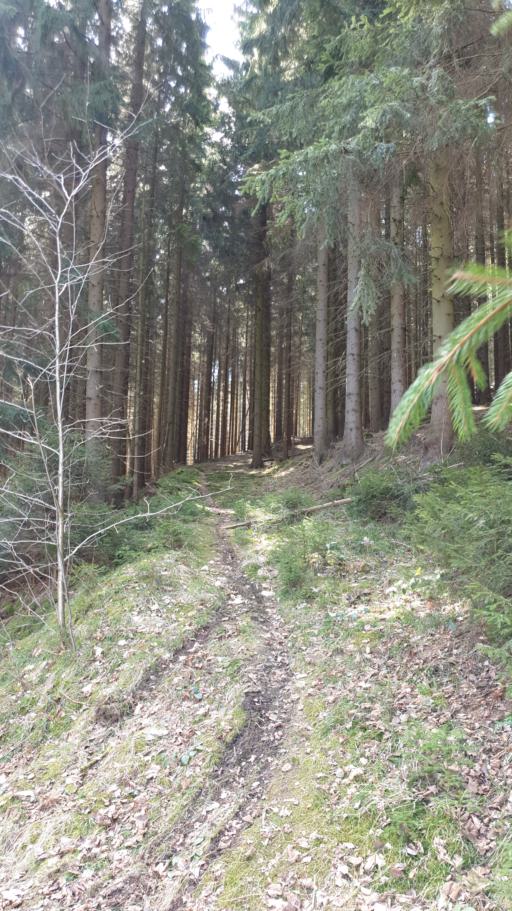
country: DE
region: Saxony
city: Gelenau
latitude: 50.7472
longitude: 12.9791
